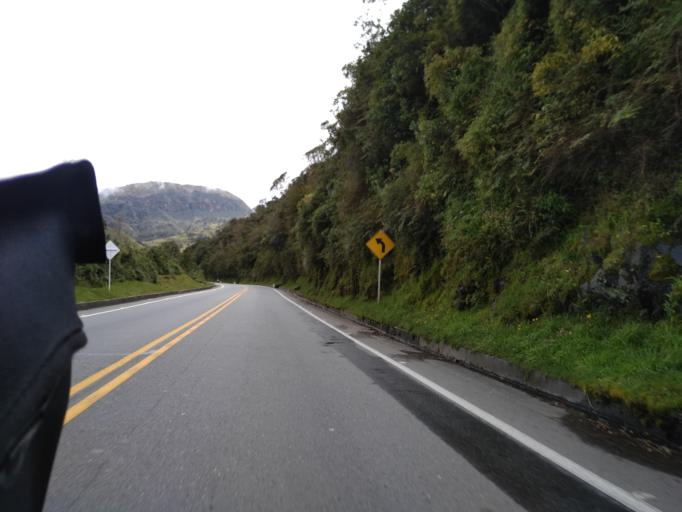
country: CO
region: Tolima
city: Herveo
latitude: 5.0257
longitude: -75.3344
